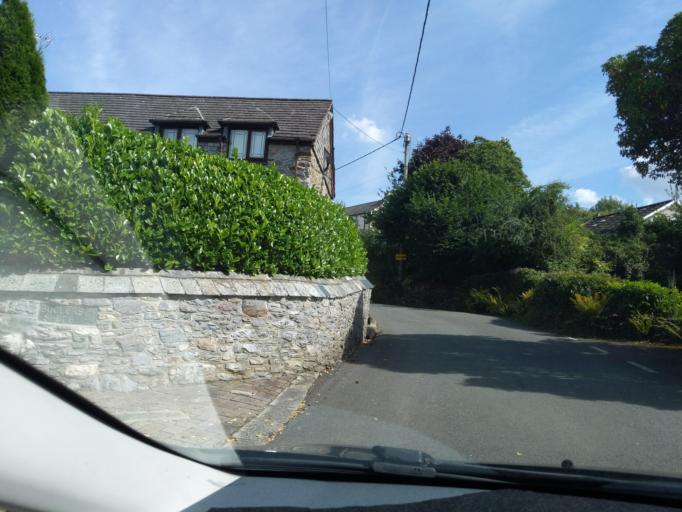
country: GB
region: England
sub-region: Cornwall
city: Torpoint
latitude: 50.3608
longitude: -4.2399
